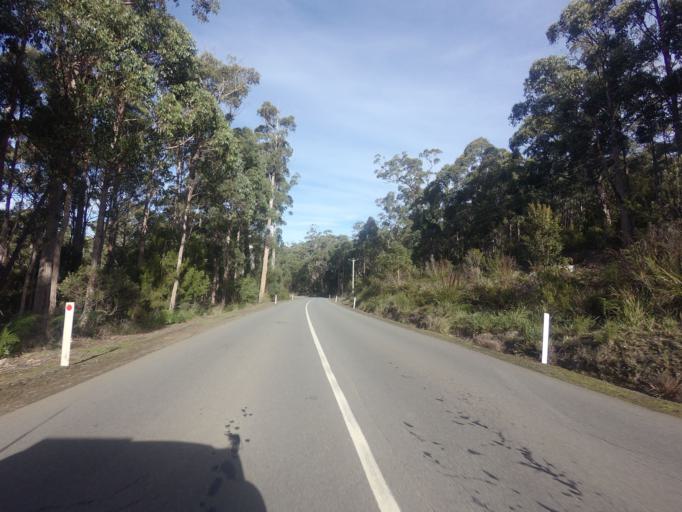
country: AU
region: Tasmania
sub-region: Clarence
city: Sandford
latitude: -43.0591
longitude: 147.8532
